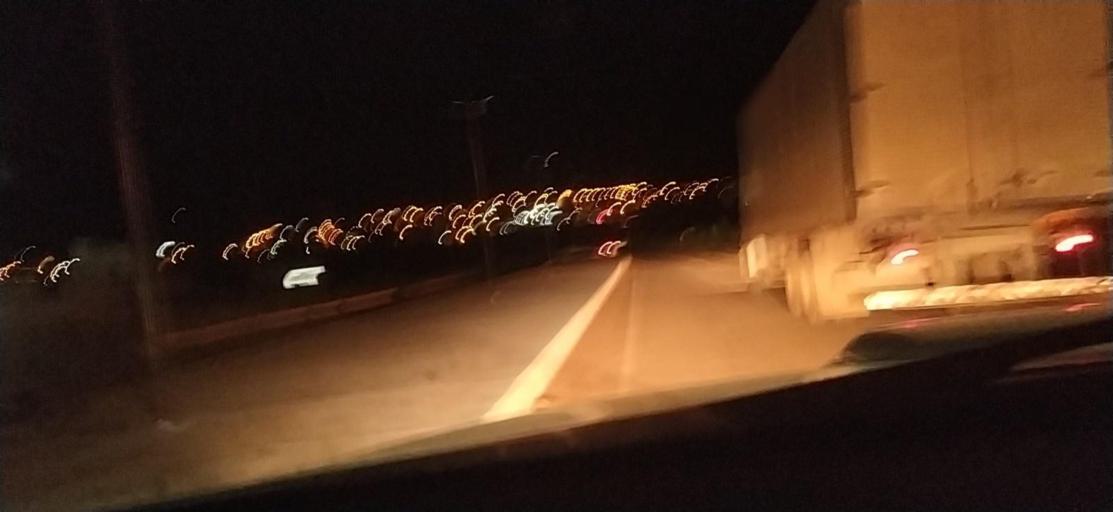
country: BR
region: Minas Gerais
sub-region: Monte Azul
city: Monte Azul
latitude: -15.1579
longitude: -42.8658
